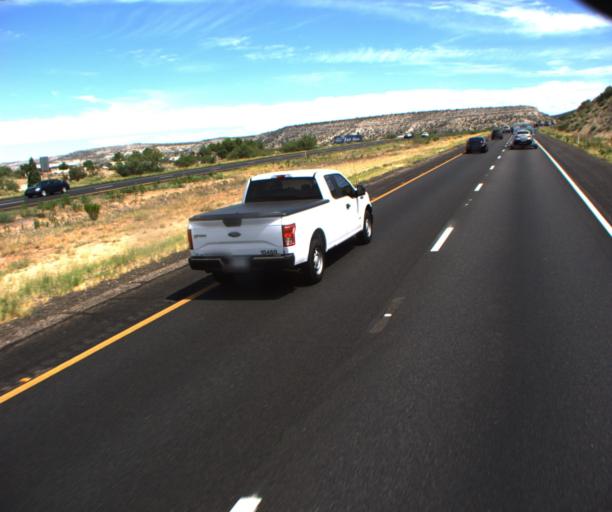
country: US
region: Arizona
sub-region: Yavapai County
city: Camp Verde
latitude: 34.6032
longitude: -111.8706
